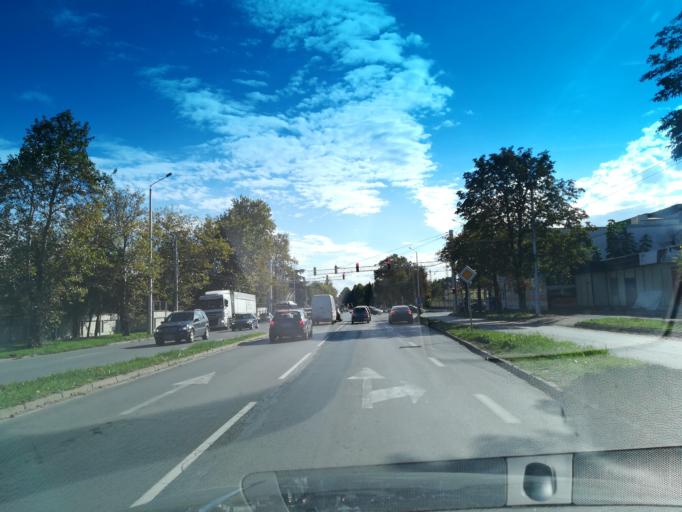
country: BG
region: Stara Zagora
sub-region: Obshtina Stara Zagora
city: Stara Zagora
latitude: 42.4105
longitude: 25.6395
